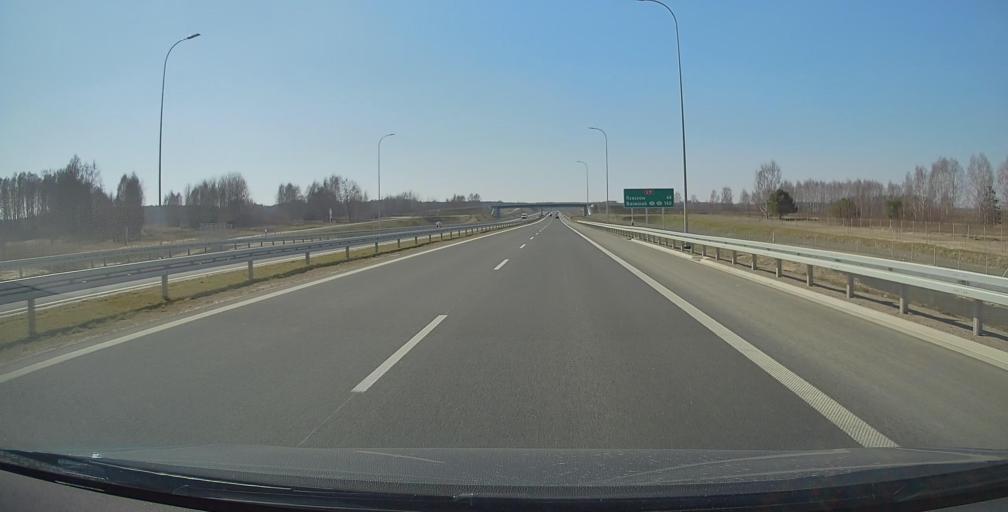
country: PL
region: Subcarpathian Voivodeship
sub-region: Powiat lezajski
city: Letownia
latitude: 50.3286
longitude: 22.1885
